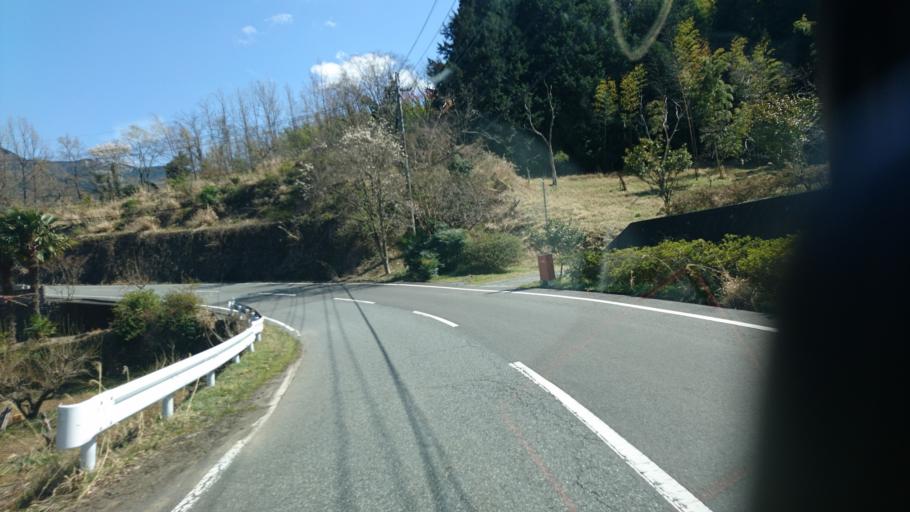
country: JP
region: Shizuoka
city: Fujinomiya
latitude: 35.3412
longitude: 138.4411
